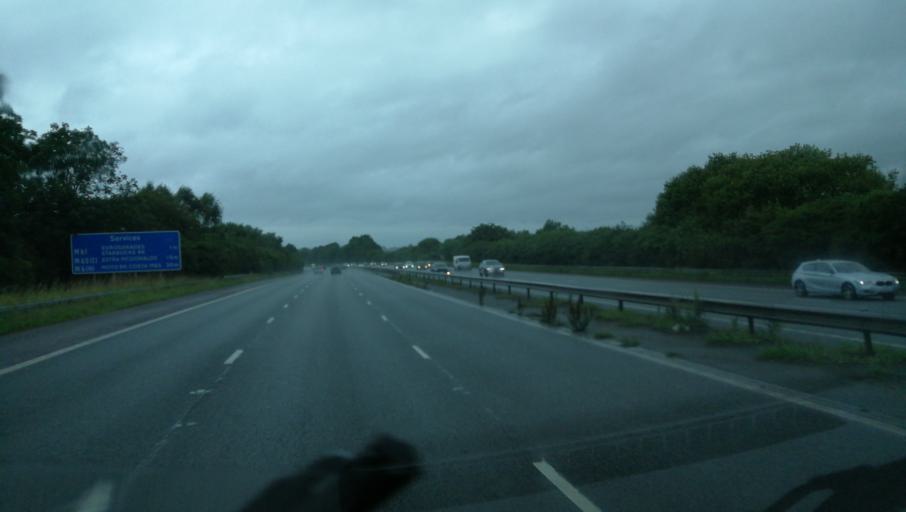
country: GB
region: England
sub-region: Borough of Bolton
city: Horwich
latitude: 53.5841
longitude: -2.5565
